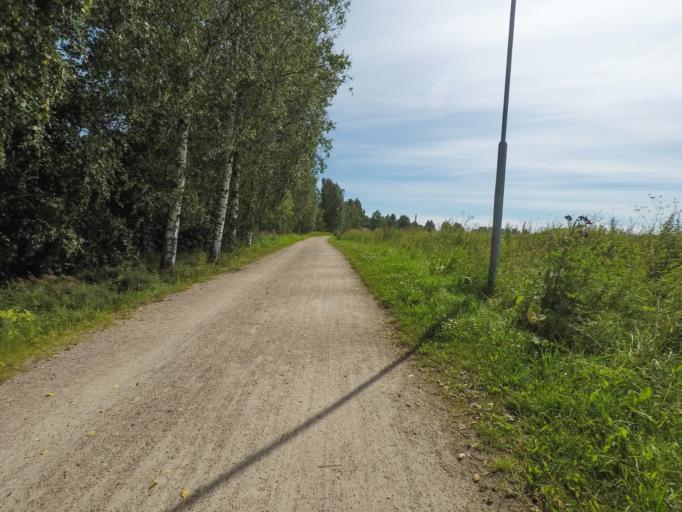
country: FI
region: Uusimaa
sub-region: Helsinki
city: Vantaa
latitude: 60.2550
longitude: 24.9770
